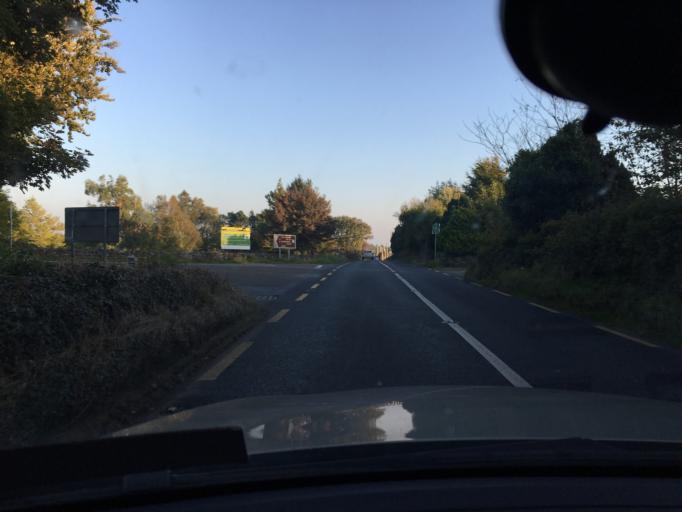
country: IE
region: Connaught
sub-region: County Galway
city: Oughterard
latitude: 53.4186
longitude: -9.2936
